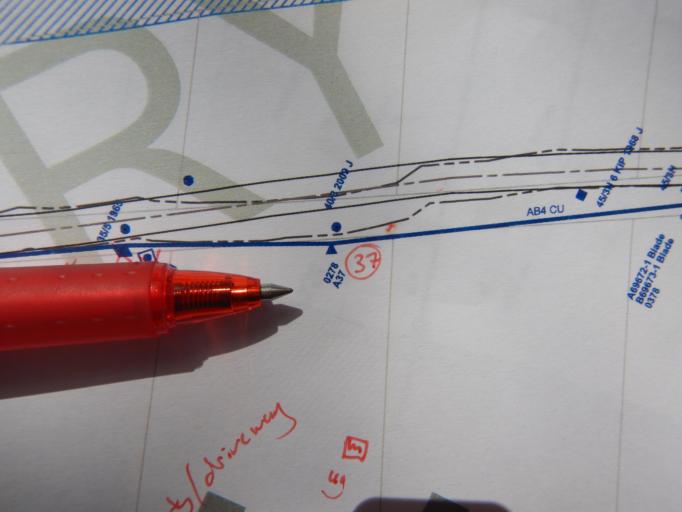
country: US
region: Florida
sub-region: Sarasota County
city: Gulf Gate Estates
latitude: 27.2336
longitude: -82.5237
